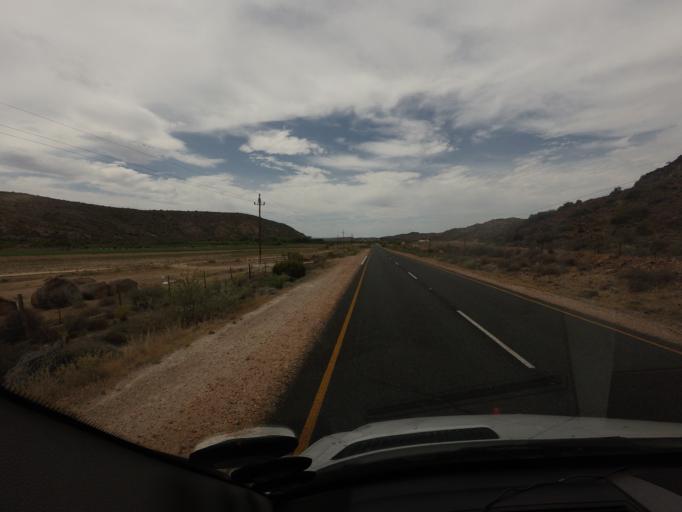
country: ZA
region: Western Cape
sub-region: Overberg District Municipality
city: Swellendam
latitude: -33.8511
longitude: 20.8316
